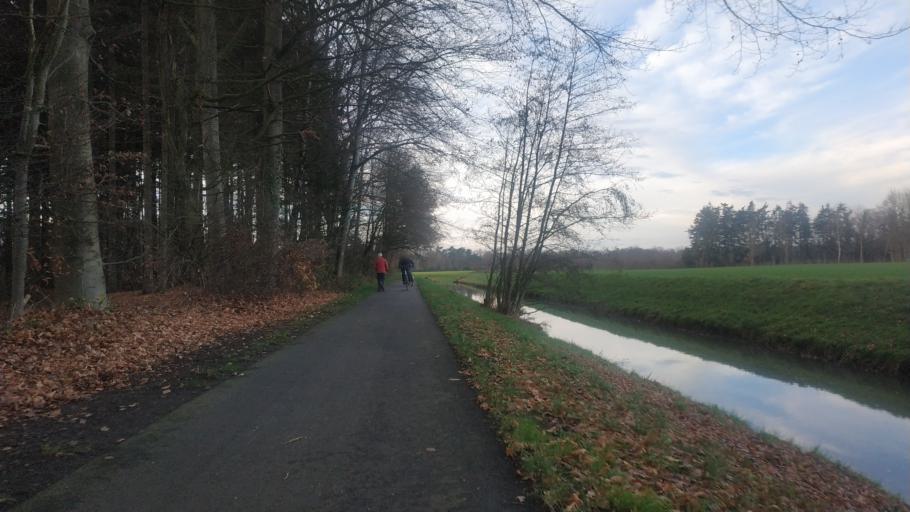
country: DE
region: North Rhine-Westphalia
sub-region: Regierungsbezirk Munster
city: Birgte
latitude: 52.2899
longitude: 7.6325
